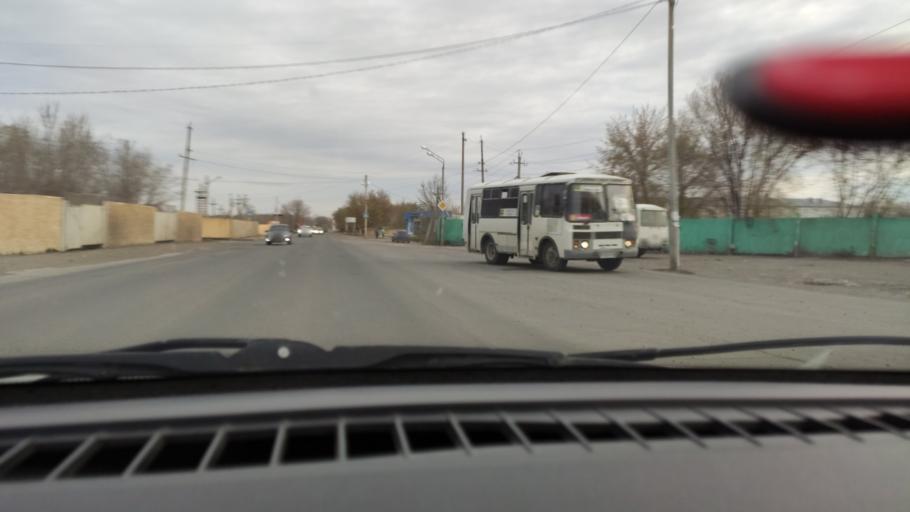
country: RU
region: Orenburg
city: Tatarskaya Kargala
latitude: 51.8826
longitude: 55.1522
